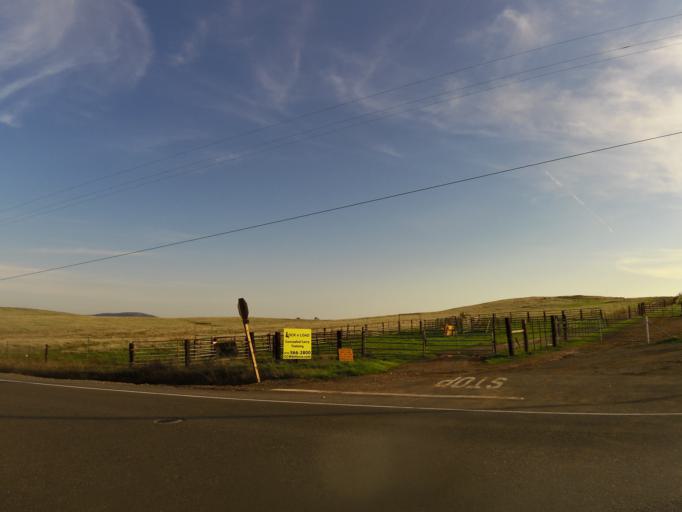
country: US
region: California
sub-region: El Dorado County
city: El Dorado Hills
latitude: 38.6221
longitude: -121.1141
